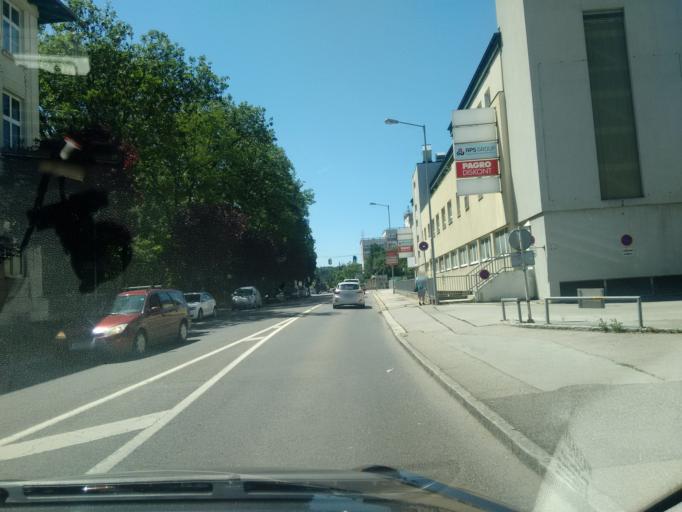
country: AT
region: Lower Austria
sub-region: Sankt Polten Stadt
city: Sankt Poelten
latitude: 48.2014
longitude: 15.6263
